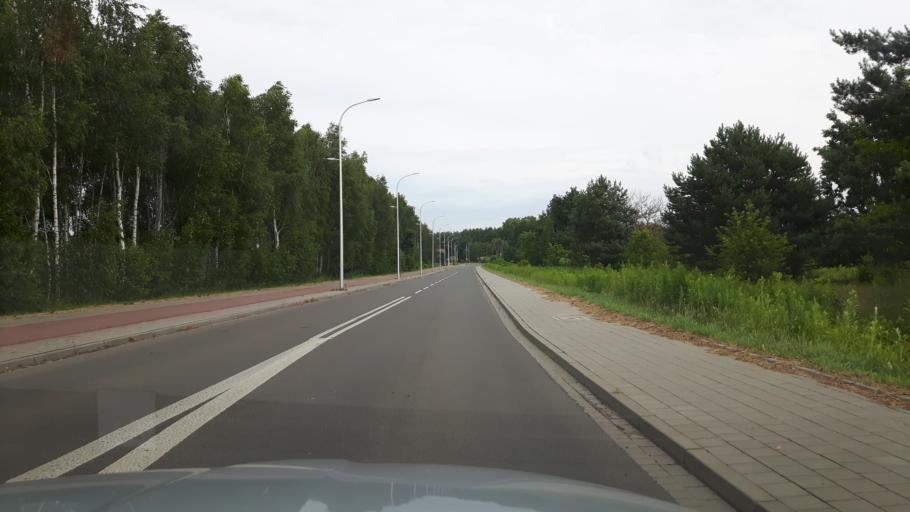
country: PL
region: Masovian Voivodeship
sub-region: Powiat wolominski
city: Wolomin
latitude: 52.3159
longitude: 21.2198
